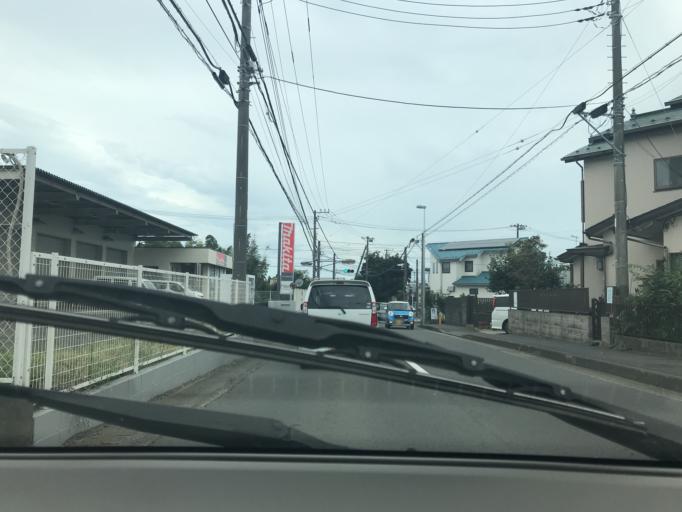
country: JP
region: Kanagawa
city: Fujisawa
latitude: 35.3868
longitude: 139.4394
